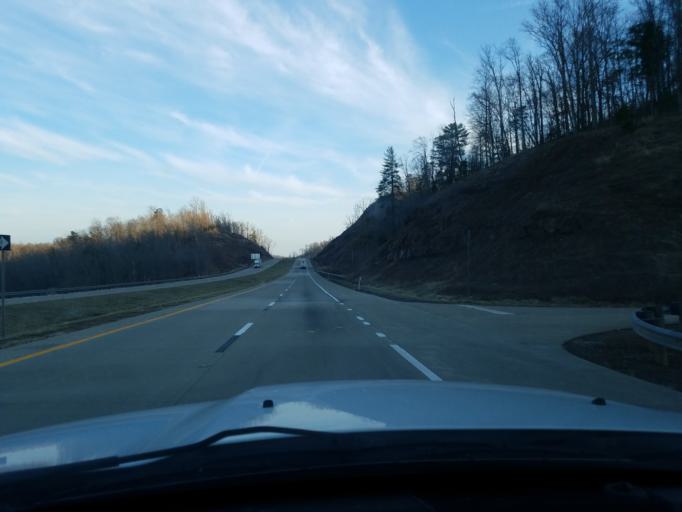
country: US
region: West Virginia
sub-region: Putnam County
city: Eleanor
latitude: 38.5121
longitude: -81.9320
